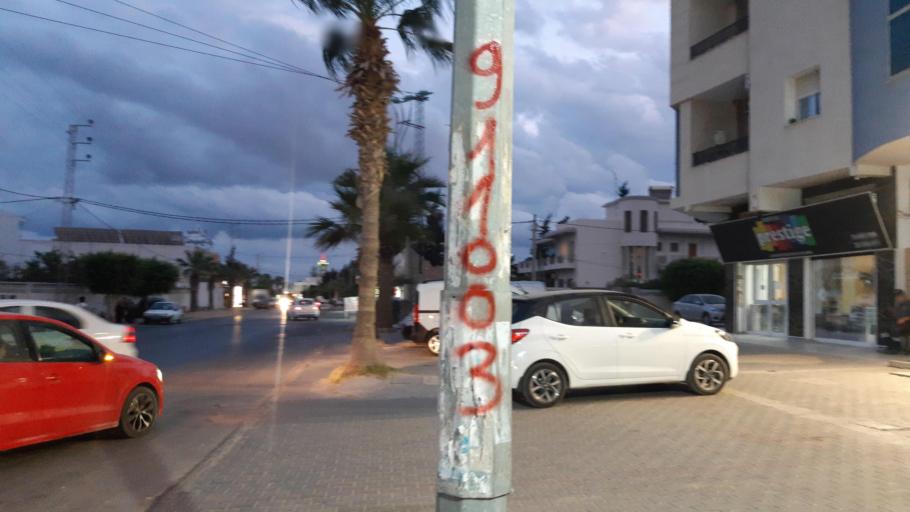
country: TN
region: Safaqis
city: Sfax
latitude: 34.7799
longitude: 10.7477
